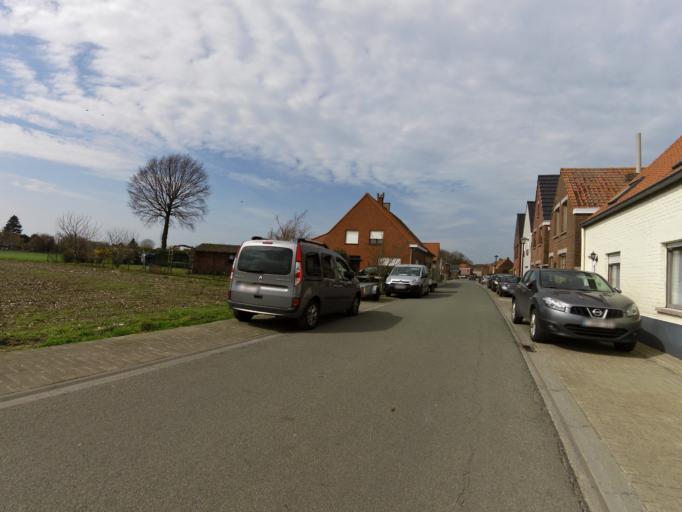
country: BE
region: Flanders
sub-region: Provincie West-Vlaanderen
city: Koekelare
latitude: 51.0856
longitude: 2.9767
